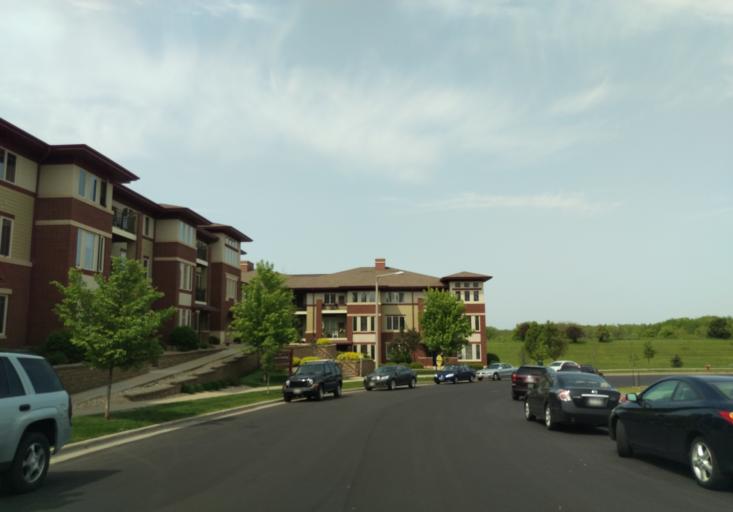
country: US
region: Wisconsin
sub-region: Dane County
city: Monona
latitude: 43.0854
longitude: -89.2815
